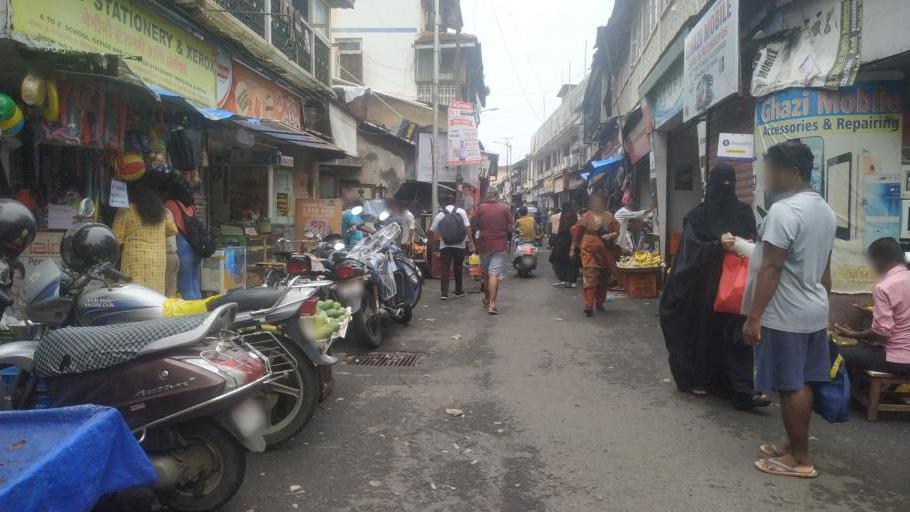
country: IN
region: Maharashtra
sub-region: Mumbai Suburban
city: Mumbai
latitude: 19.0541
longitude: 72.8328
